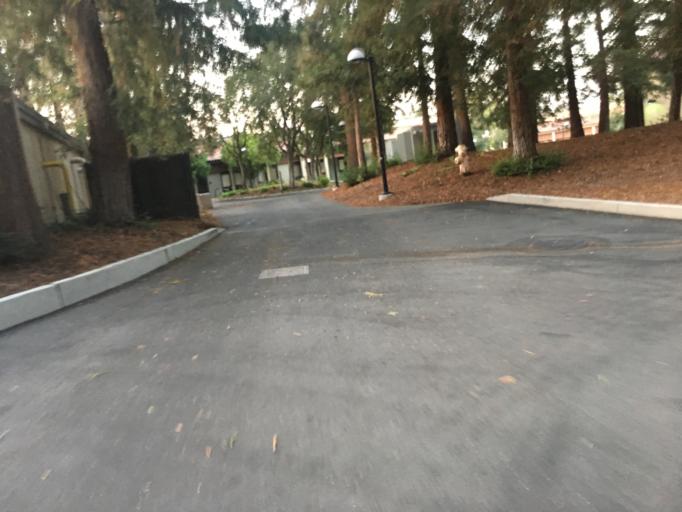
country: US
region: California
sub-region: Santa Clara County
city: Cupertino
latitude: 37.3192
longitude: -122.0459
